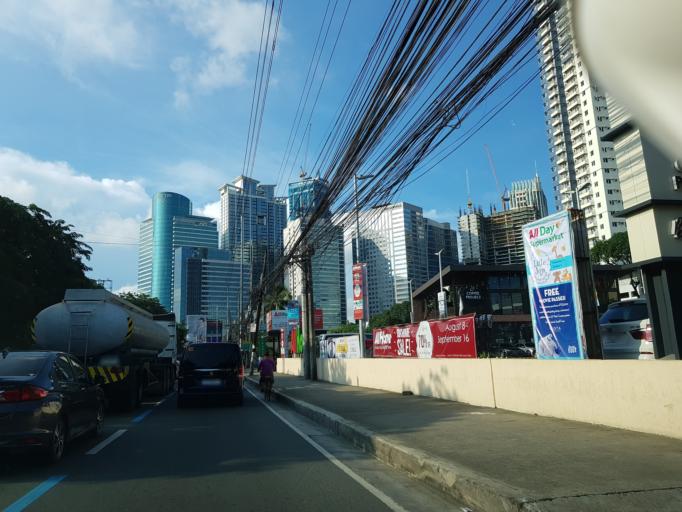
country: PH
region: Metro Manila
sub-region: Marikina
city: Calumpang
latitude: 14.6035
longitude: 121.0794
